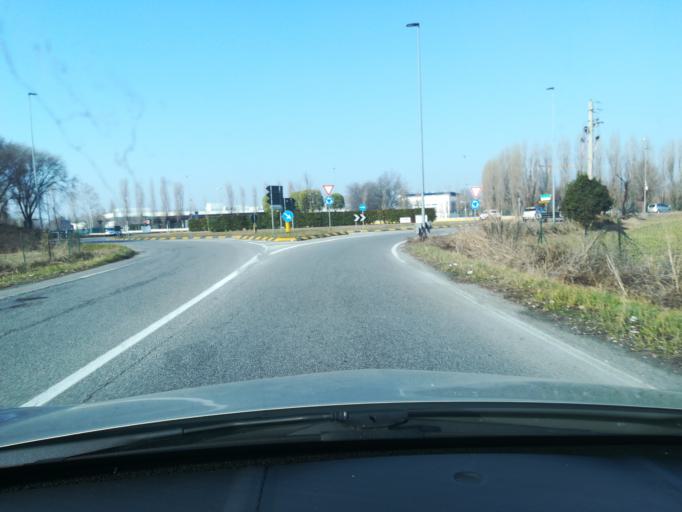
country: IT
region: Lombardy
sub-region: Provincia di Bergamo
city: Stezzano
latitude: 45.6570
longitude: 9.6570
